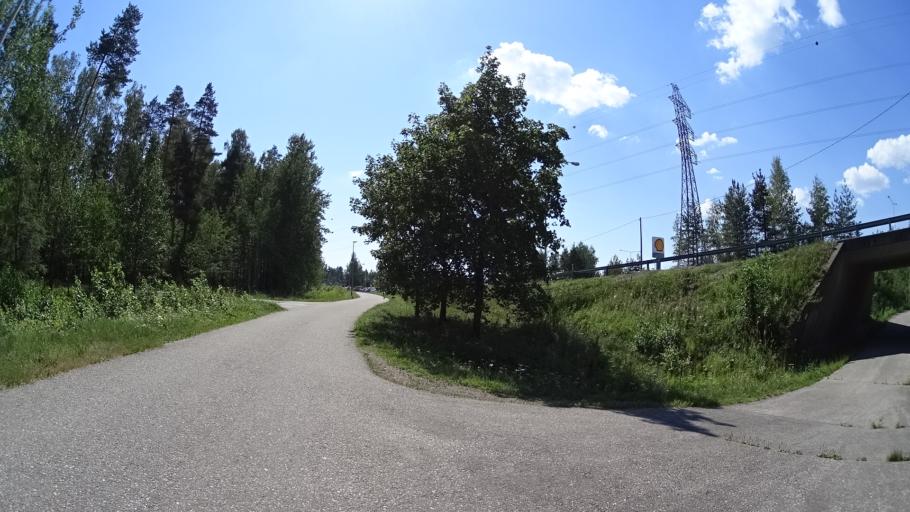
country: FI
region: Uusimaa
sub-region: Helsinki
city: Vantaa
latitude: 60.3099
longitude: 24.9993
